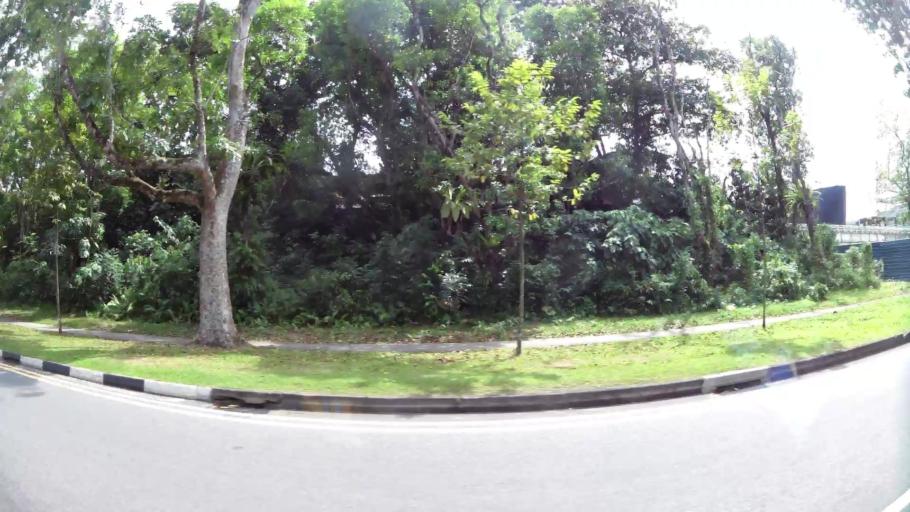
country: MY
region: Johor
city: Johor Bahru
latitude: 1.4103
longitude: 103.7644
